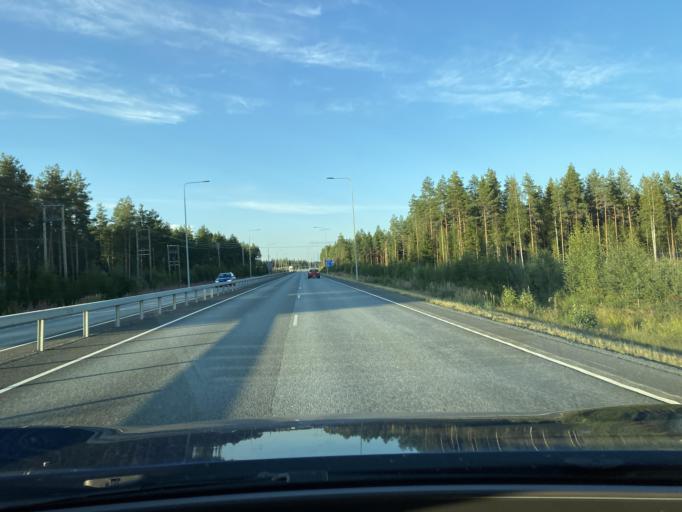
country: FI
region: Southern Ostrobothnia
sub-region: Seinaejoki
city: Seinaejoki
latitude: 62.7284
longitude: 22.8864
